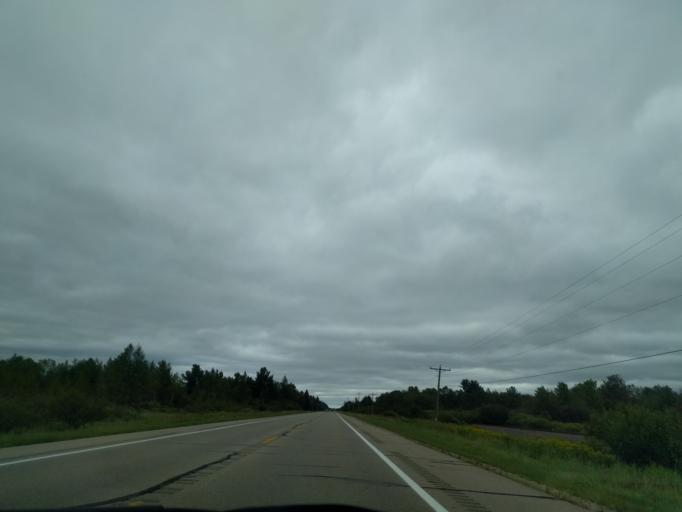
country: US
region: Michigan
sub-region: Delta County
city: Gladstone
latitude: 45.8867
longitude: -87.0655
